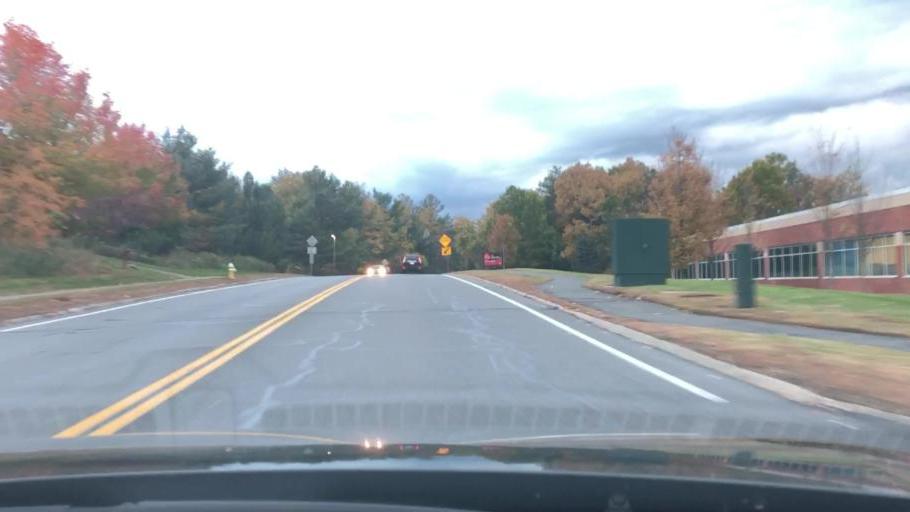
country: US
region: Massachusetts
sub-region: Middlesex County
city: Chelmsford
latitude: 42.6278
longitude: -71.3620
